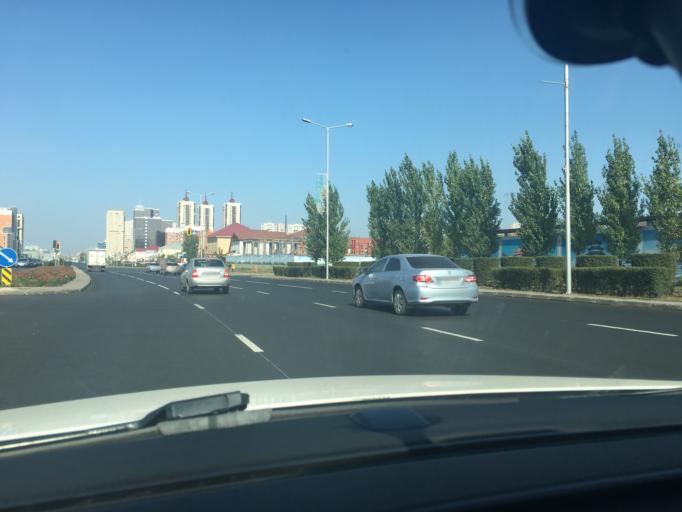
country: KZ
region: Astana Qalasy
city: Astana
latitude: 51.1308
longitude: 71.4711
